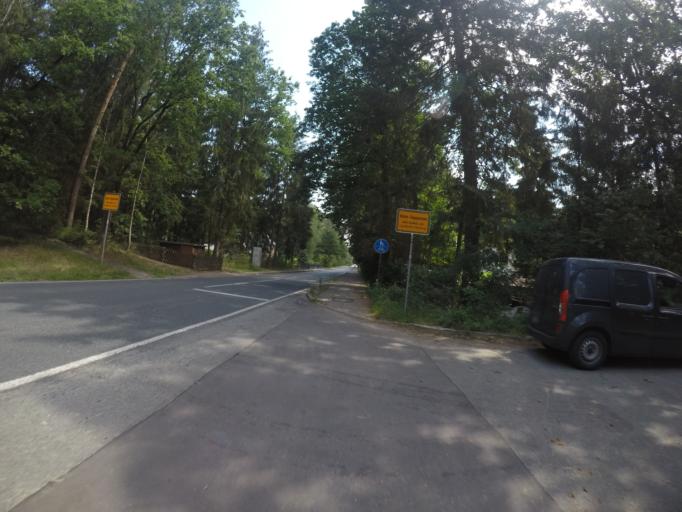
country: DE
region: Lower Saxony
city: Handeloh
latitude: 53.2870
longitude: 9.8491
